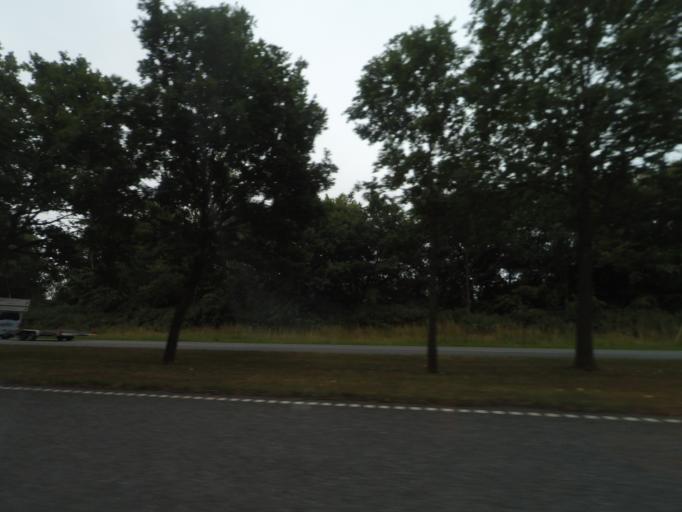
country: DK
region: South Denmark
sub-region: Odense Kommune
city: Stige
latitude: 55.4454
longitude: 10.3769
